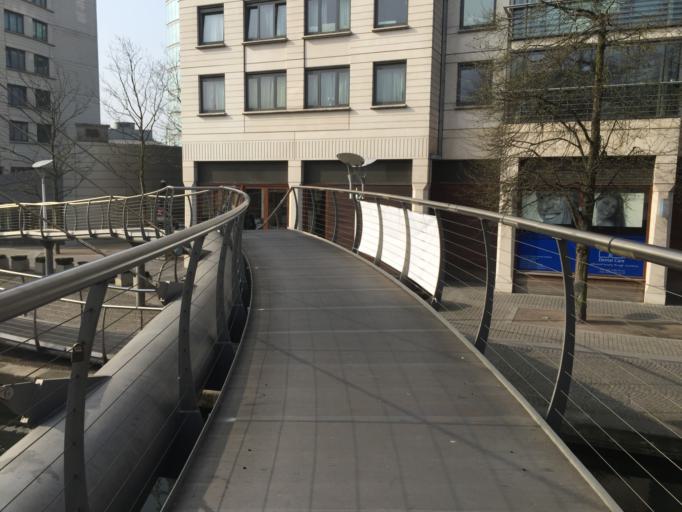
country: GB
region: England
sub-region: Greater London
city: Bayswater
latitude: 51.5198
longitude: -0.1796
